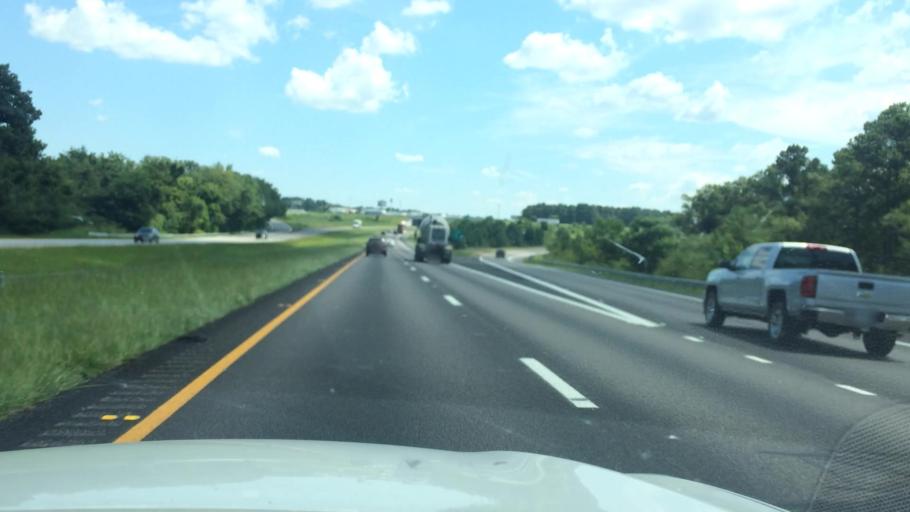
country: US
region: South Carolina
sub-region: Aiken County
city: Belvedere
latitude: 33.5607
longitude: -81.9420
